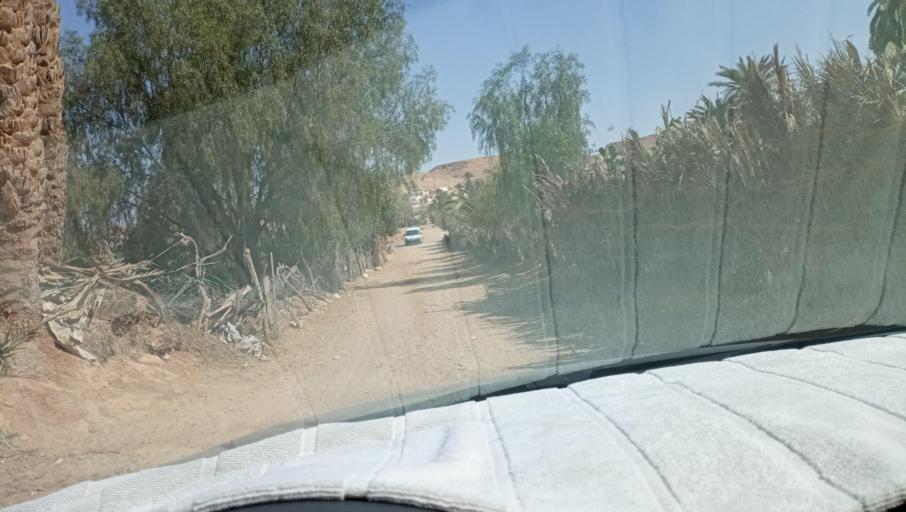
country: TN
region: Tataouine
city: Tataouine
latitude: 32.9791
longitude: 10.3849
